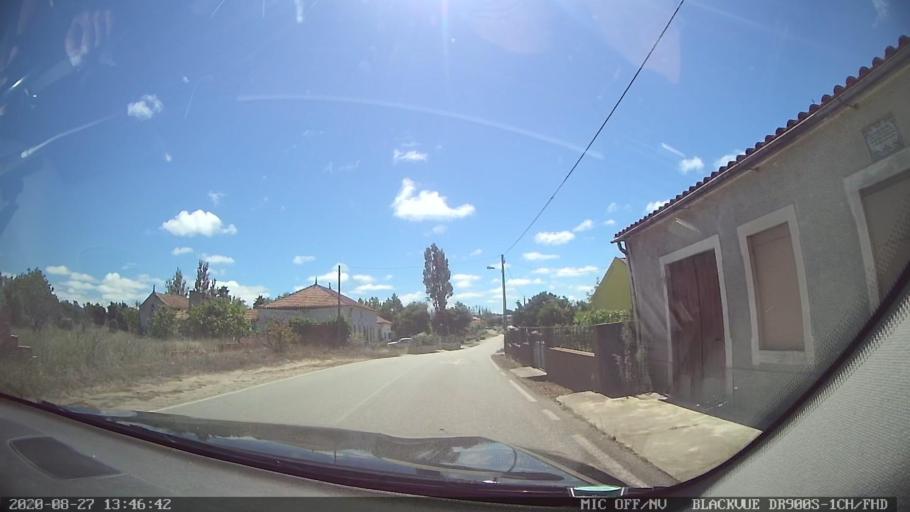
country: PT
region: Coimbra
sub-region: Mira
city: Mira
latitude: 40.3940
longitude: -8.7360
